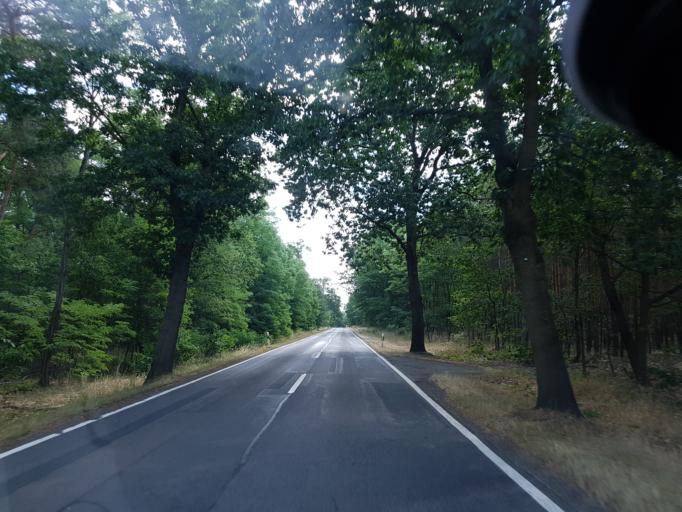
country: DE
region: Brandenburg
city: Drebkau
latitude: 51.6638
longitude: 14.1929
